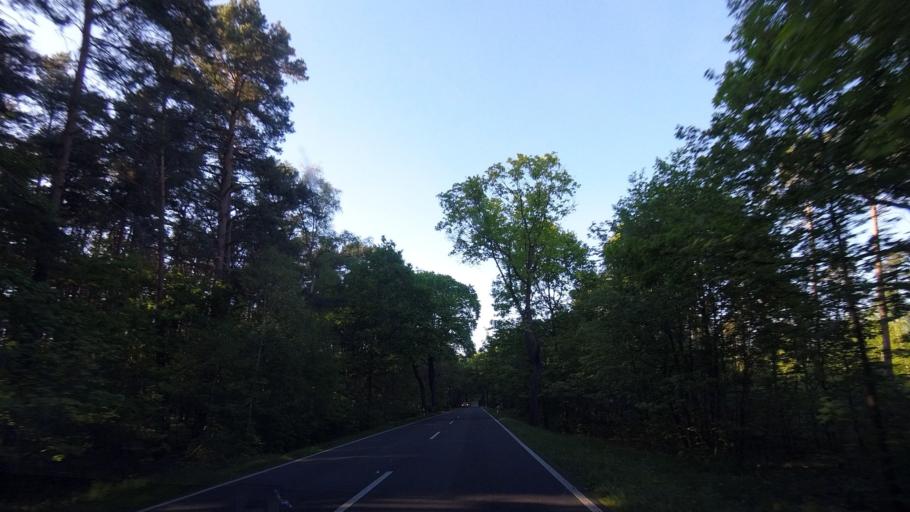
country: DE
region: Brandenburg
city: Golssen
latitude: 51.9931
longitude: 13.5596
